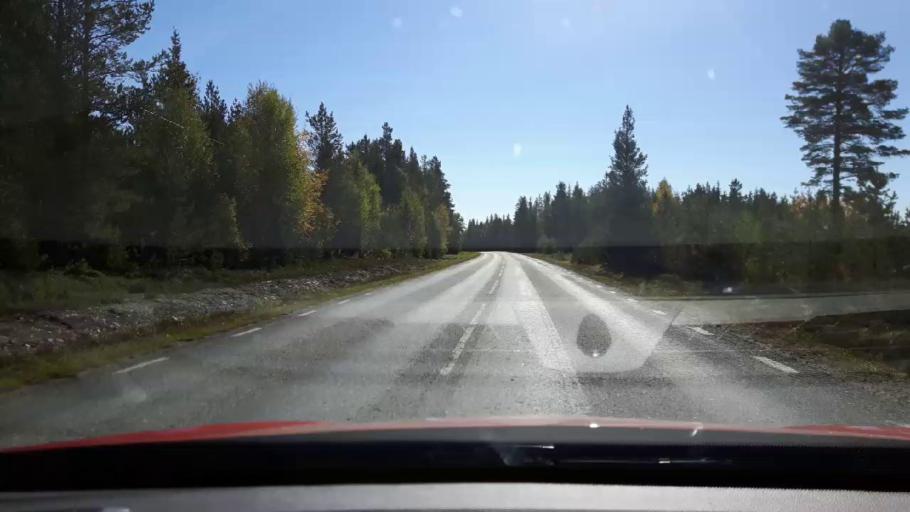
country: SE
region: Jaemtland
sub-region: Harjedalens Kommun
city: Sveg
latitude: 62.4342
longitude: 13.8822
